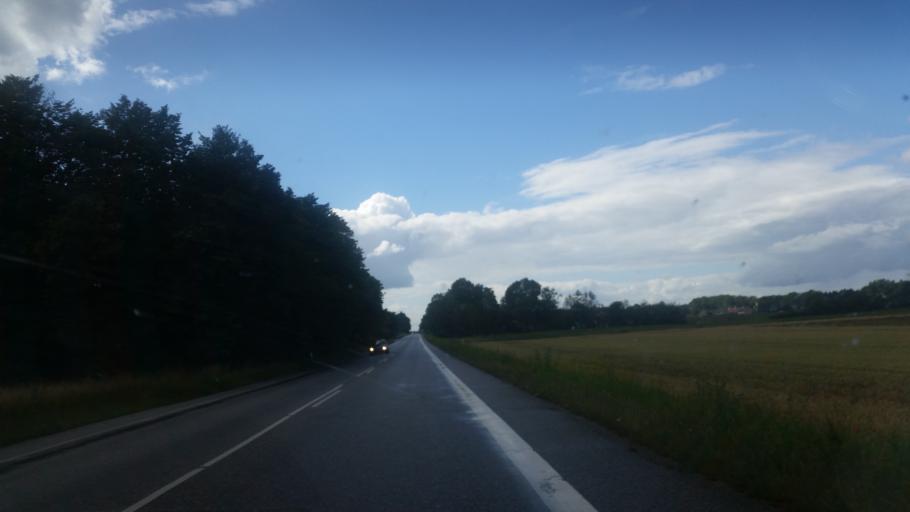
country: DK
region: Zealand
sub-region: Holbaek Kommune
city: Holbaek
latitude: 55.7213
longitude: 11.6005
